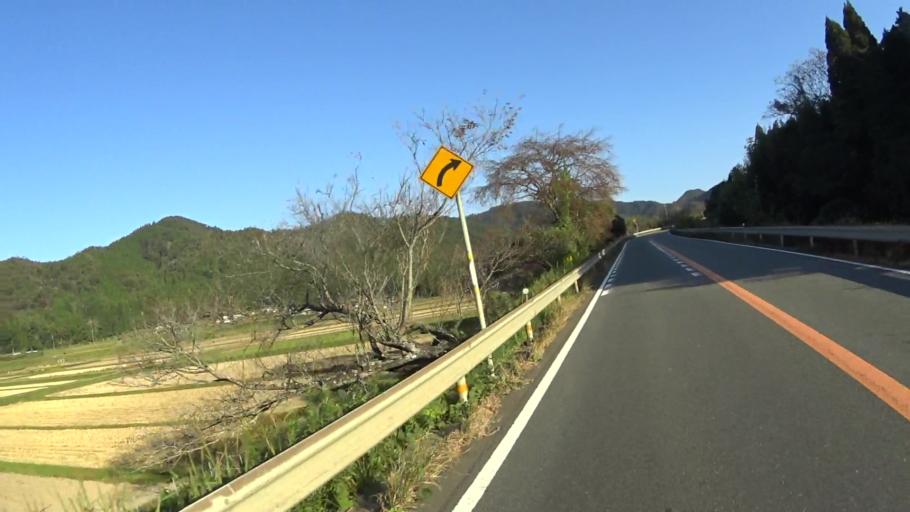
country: JP
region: Kyoto
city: Ayabe
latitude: 35.2489
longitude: 135.2132
